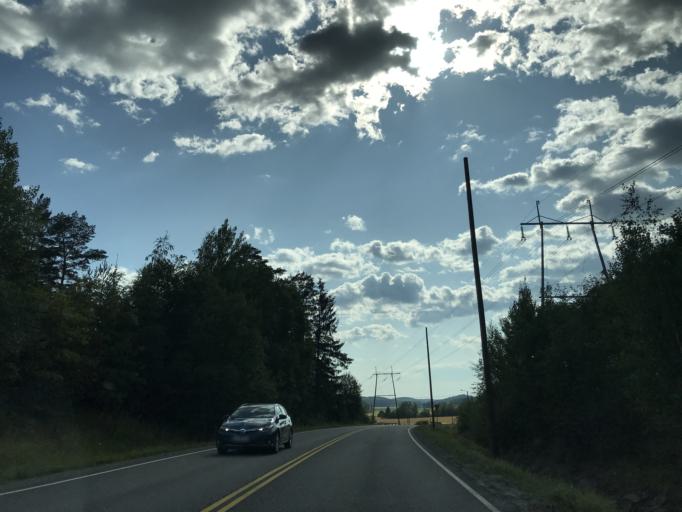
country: FI
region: Uusimaa
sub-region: Helsinki
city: Nurmijaervi
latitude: 60.4486
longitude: 24.6975
